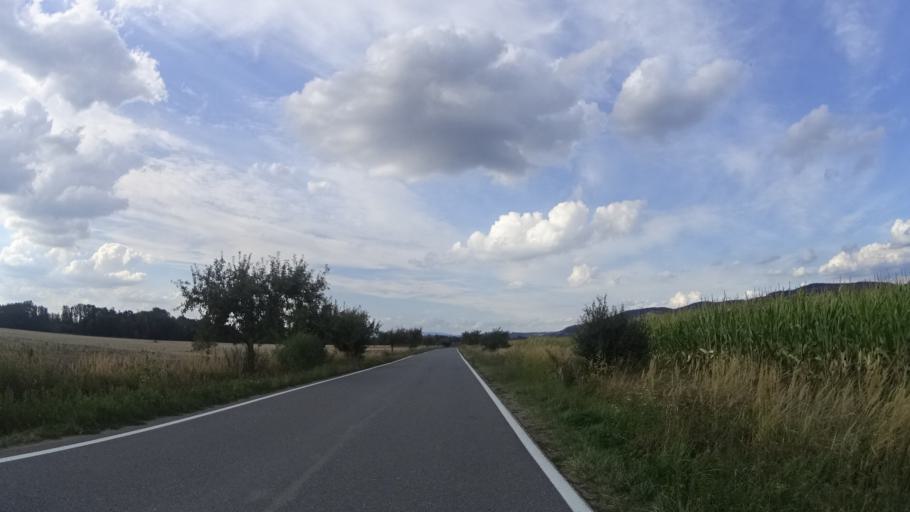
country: CZ
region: Olomoucky
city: Dubicko
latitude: 49.8332
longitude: 16.9360
